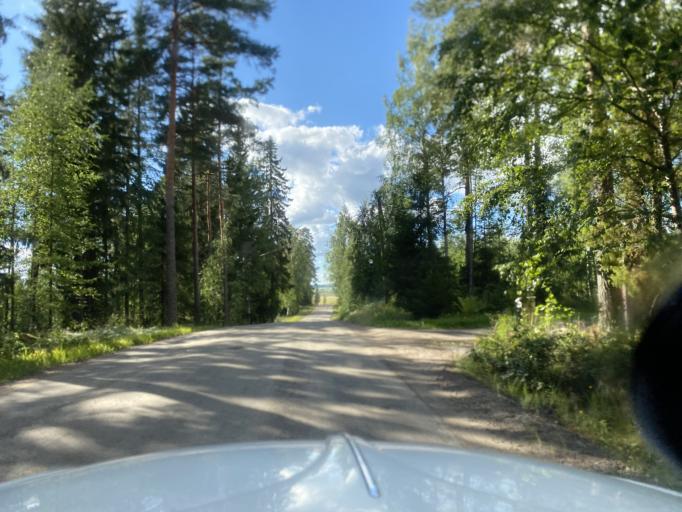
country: FI
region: Pirkanmaa
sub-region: Lounais-Pirkanmaa
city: Punkalaidun
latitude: 61.1396
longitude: 23.2122
